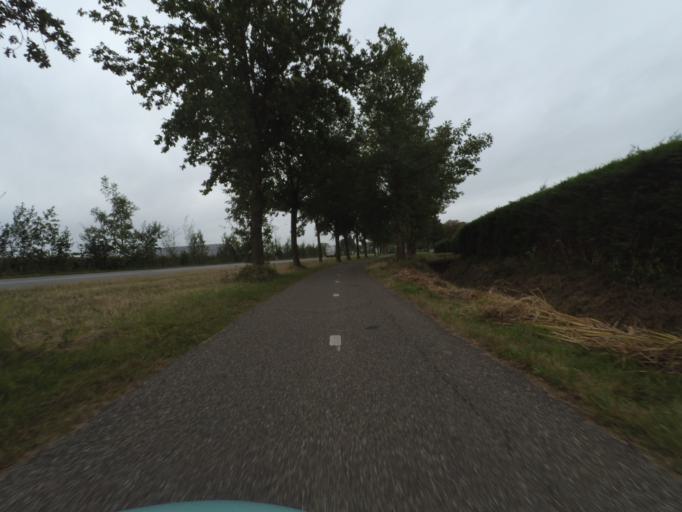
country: NL
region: Gelderland
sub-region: Gemeente Geldermalsen
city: Geldermalsen
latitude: 51.9196
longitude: 5.3289
